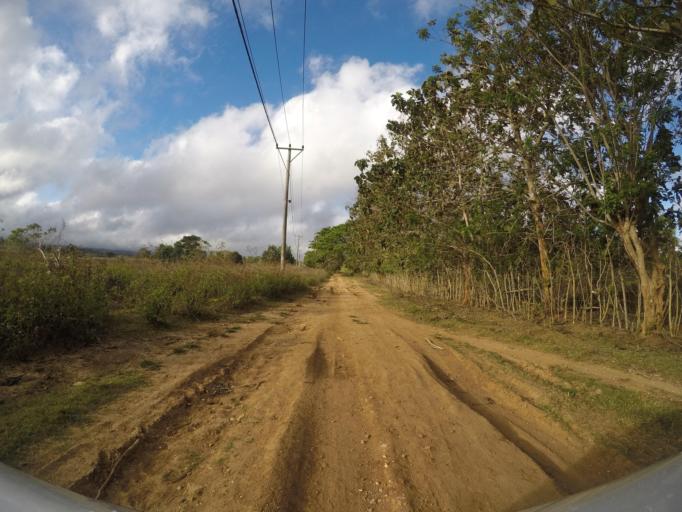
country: TL
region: Lautem
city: Lospalos
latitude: -8.5090
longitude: 126.9935
